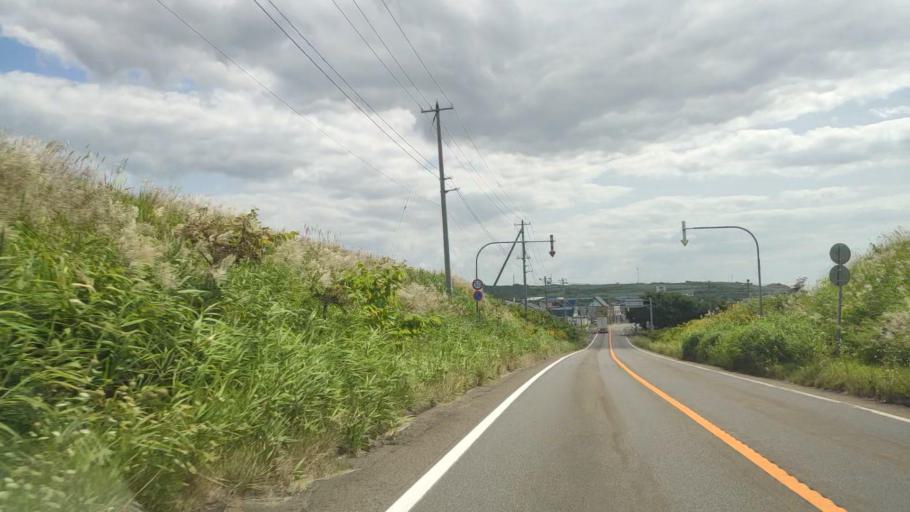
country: JP
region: Hokkaido
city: Rumoi
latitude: 44.5374
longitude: 141.7669
